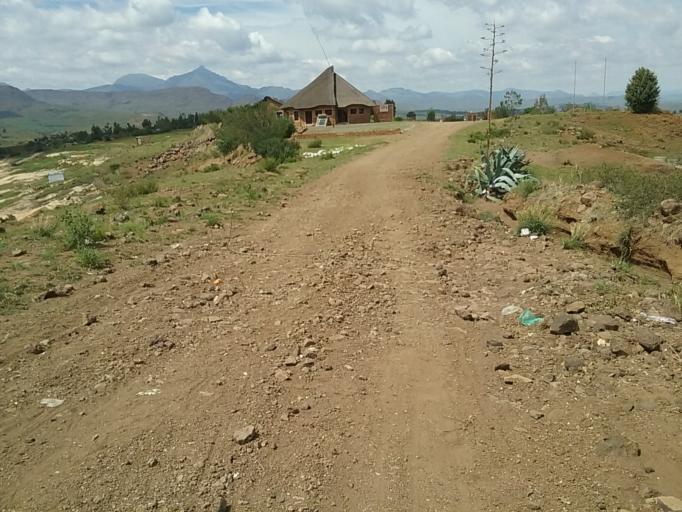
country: LS
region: Berea
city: Teyateyaneng
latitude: -29.2433
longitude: 27.8668
